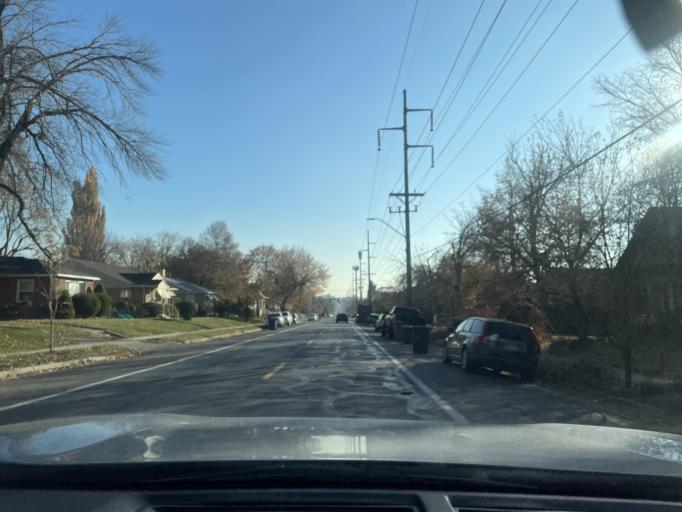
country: US
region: Utah
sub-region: Salt Lake County
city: Salt Lake City
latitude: 40.7435
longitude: -111.8597
